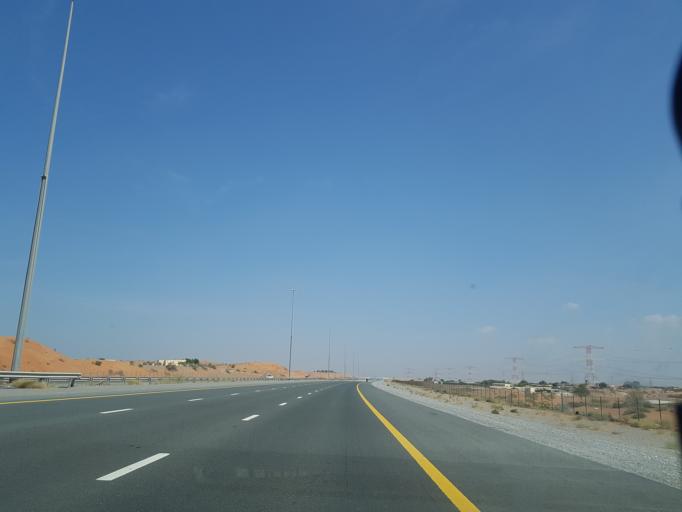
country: AE
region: Ra's al Khaymah
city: Ras al-Khaimah
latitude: 25.6789
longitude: 55.9045
